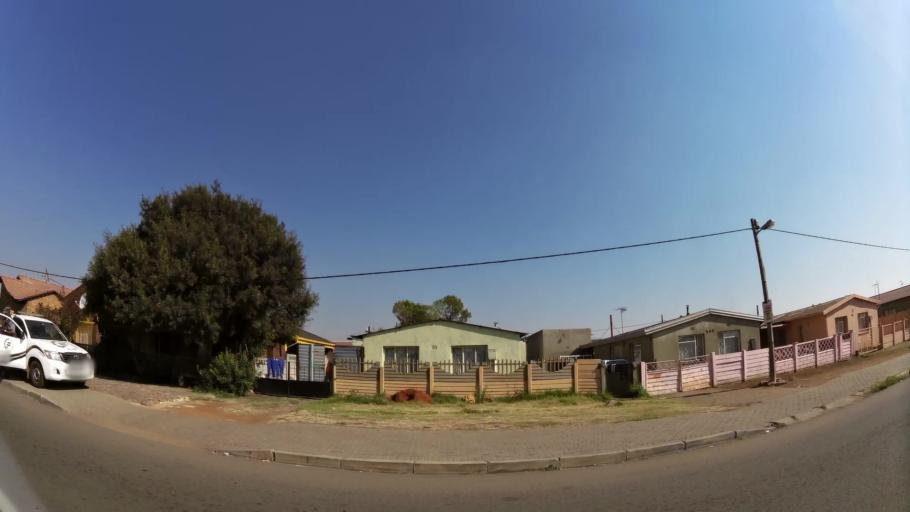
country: ZA
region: Gauteng
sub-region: Ekurhuleni Metropolitan Municipality
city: Boksburg
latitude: -26.2170
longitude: 28.2938
